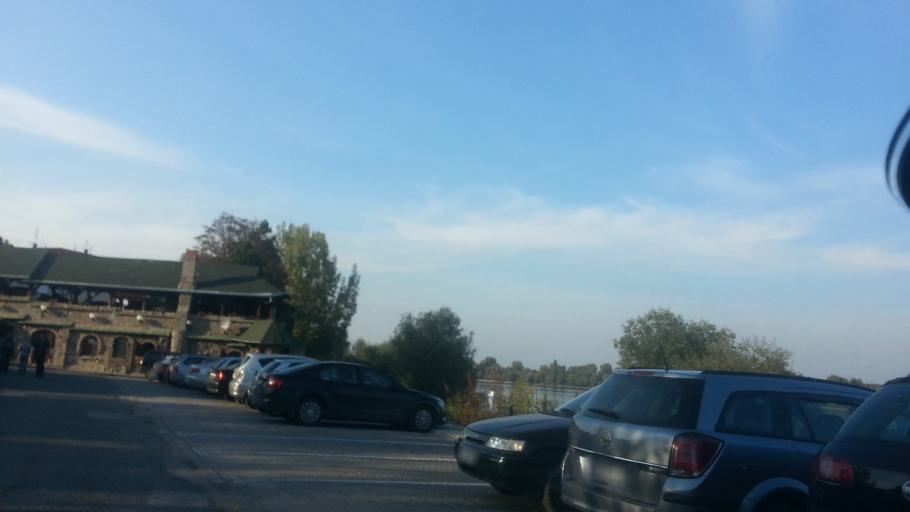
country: RS
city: Novi Slankamen
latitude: 45.1402
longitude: 20.2603
